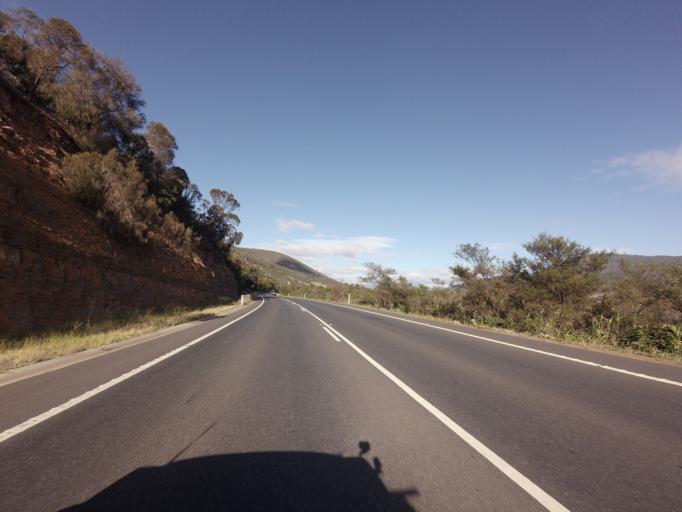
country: AU
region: Tasmania
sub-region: Glenorchy
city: Granton
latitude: -42.7474
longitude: 147.1775
